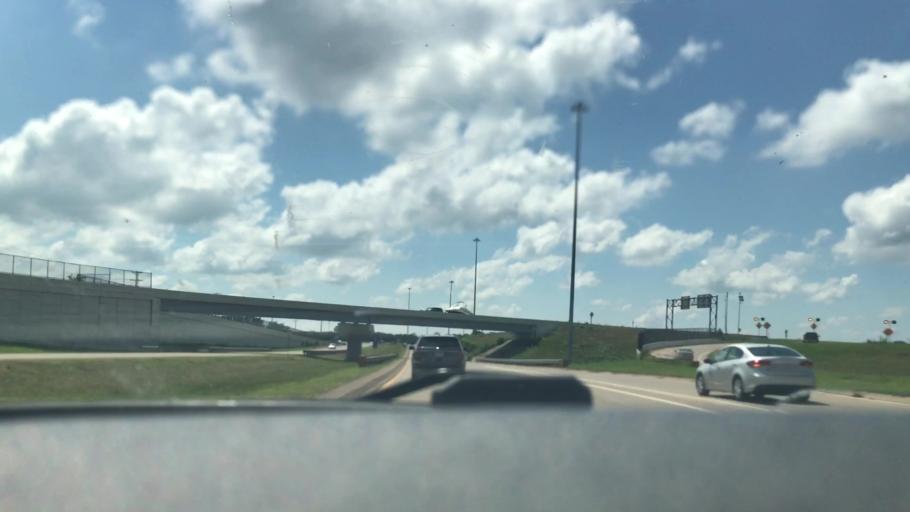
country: US
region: Wisconsin
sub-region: Eau Claire County
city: Altoona
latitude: 44.7911
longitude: -91.4548
